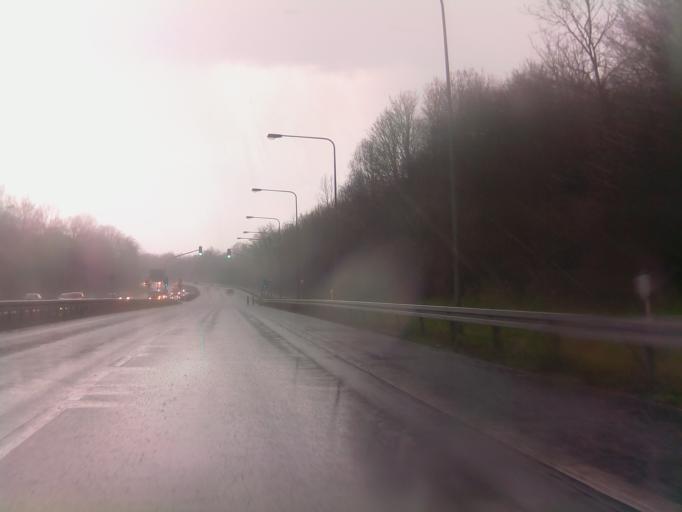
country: DE
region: Hesse
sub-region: Regierungsbezirk Darmstadt
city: Bad Vilbel
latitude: 50.1603
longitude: 8.7254
